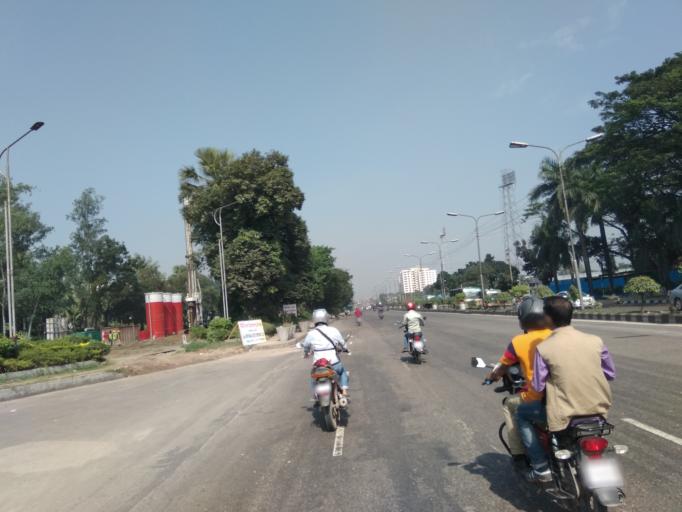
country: BD
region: Dhaka
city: Paltan
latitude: 23.8033
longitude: 90.4023
